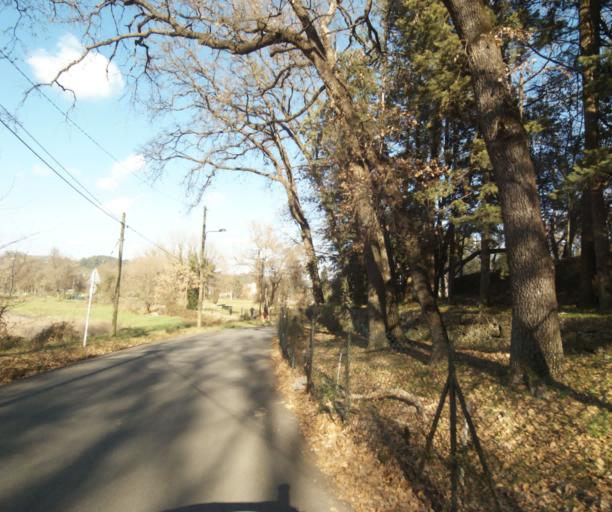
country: FR
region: Provence-Alpes-Cote d'Azur
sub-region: Departement des Alpes-Maritimes
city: Biot
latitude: 43.6148
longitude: 7.1033
